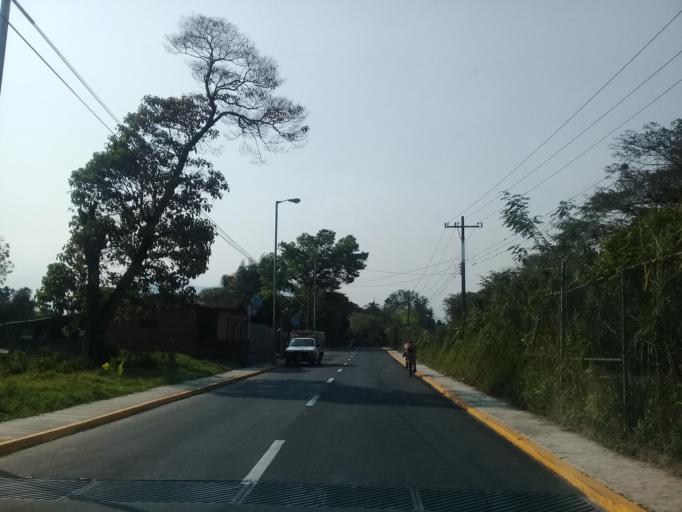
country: MX
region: Veracruz
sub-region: Ixtaczoquitlan
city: Campo Chico
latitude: 18.8504
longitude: -97.0373
